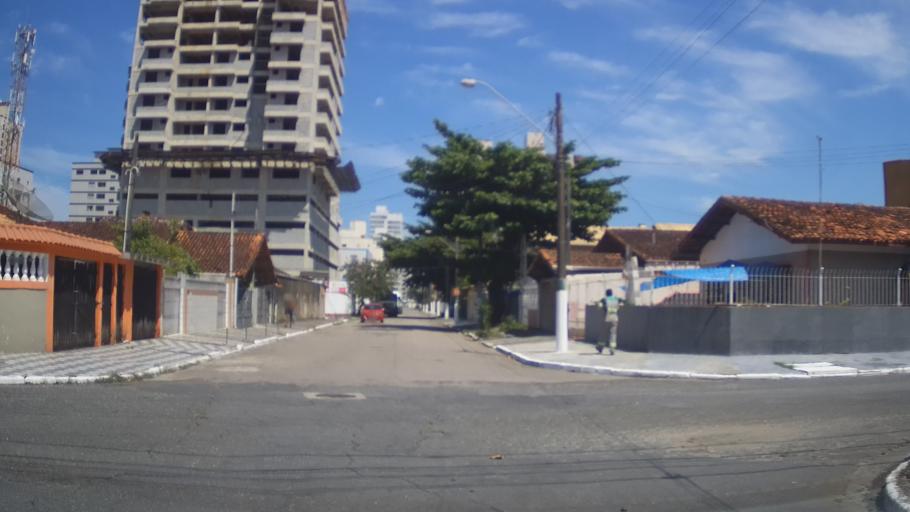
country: BR
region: Sao Paulo
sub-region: Praia Grande
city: Praia Grande
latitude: -24.0237
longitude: -46.4679
